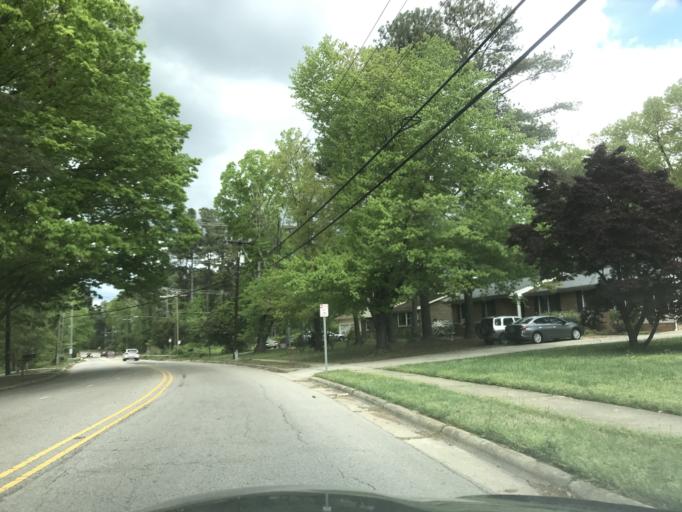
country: US
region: North Carolina
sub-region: Wake County
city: West Raleigh
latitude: 35.7729
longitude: -78.7150
